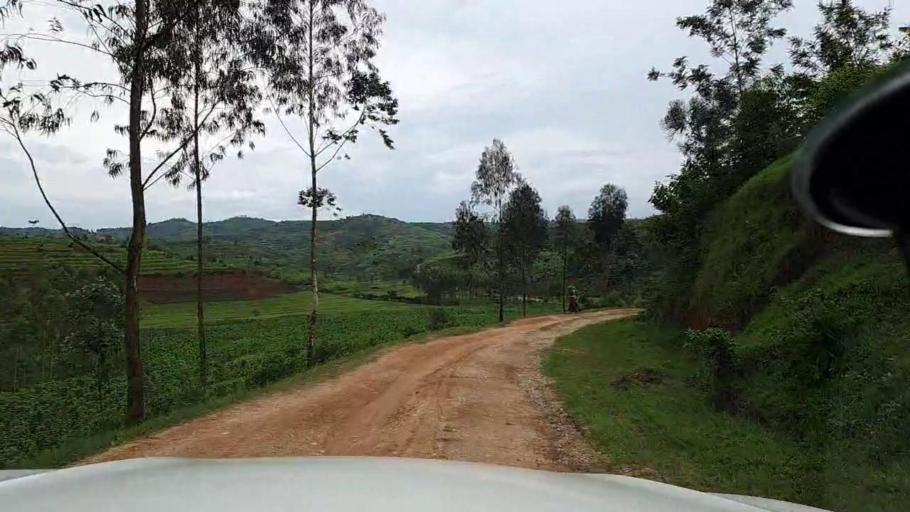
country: RW
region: Southern Province
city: Gitarama
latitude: -2.0927
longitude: 29.6411
